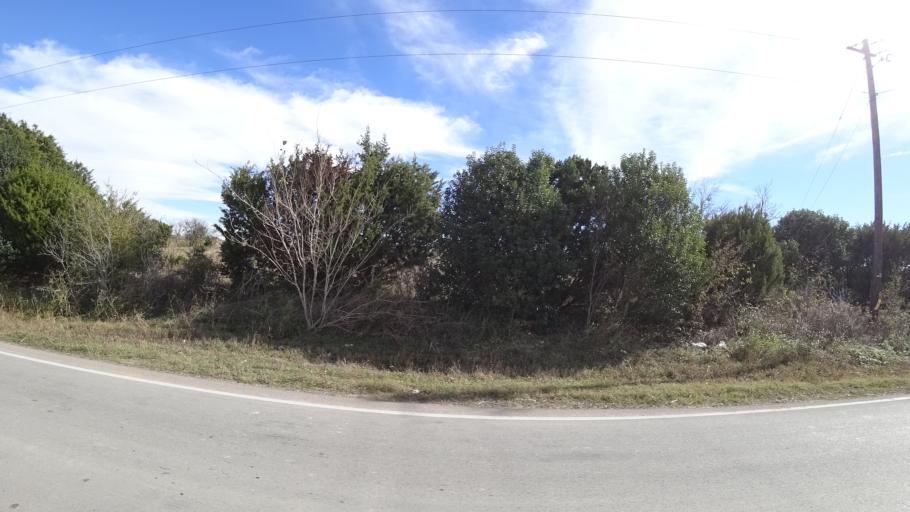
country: US
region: Texas
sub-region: Travis County
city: Onion Creek
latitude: 30.1154
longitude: -97.7467
